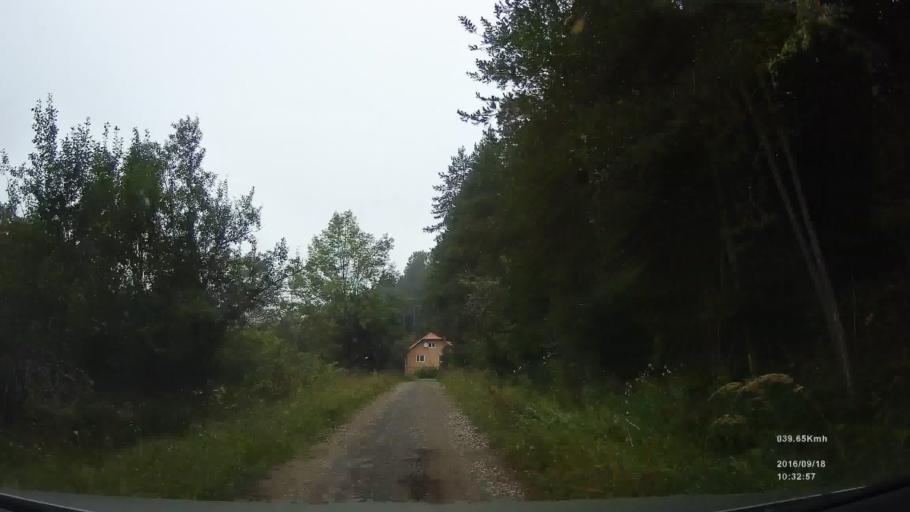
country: SK
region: Presovsky
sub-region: Okres Presov
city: Levoca
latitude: 48.9677
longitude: 20.6208
